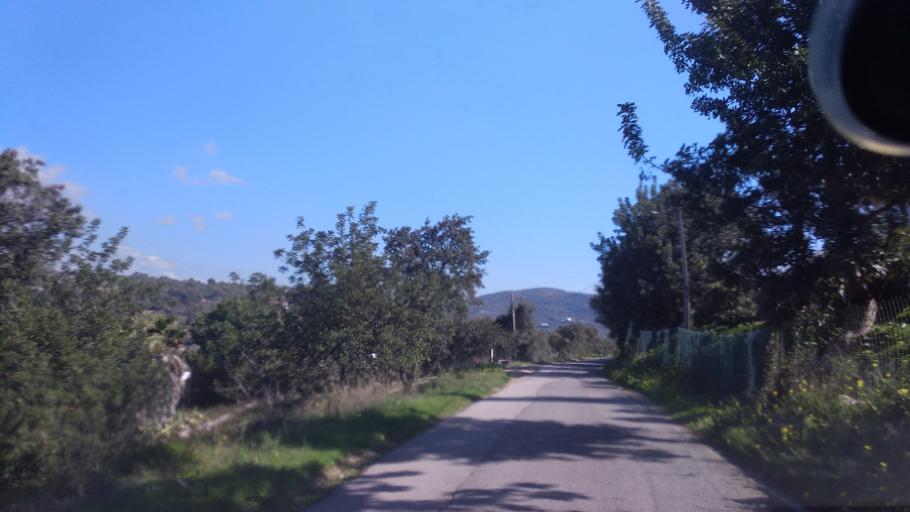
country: PT
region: Faro
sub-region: Faro
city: Santa Barbara de Nexe
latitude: 37.1116
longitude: -7.9228
